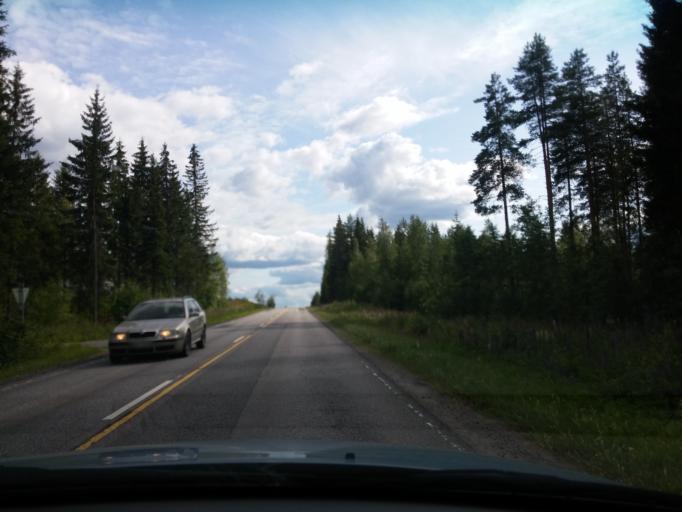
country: FI
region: Central Finland
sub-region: Keuruu
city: Keuruu
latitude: 62.3272
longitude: 24.7333
